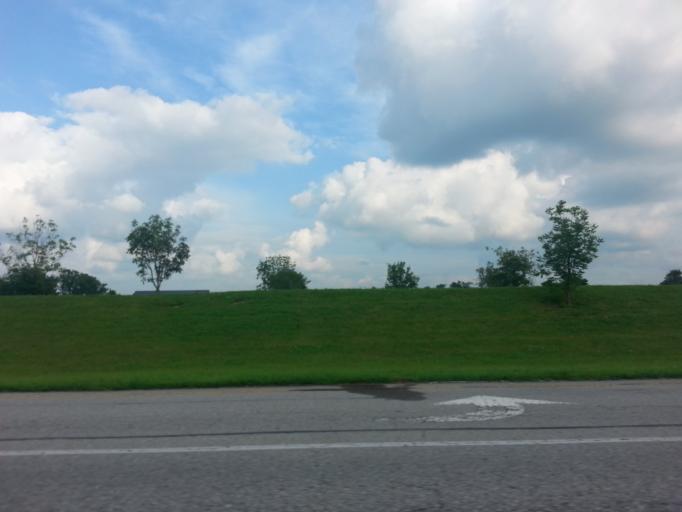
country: US
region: Kentucky
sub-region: Bourbon County
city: Paris
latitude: 38.1418
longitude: -84.3565
